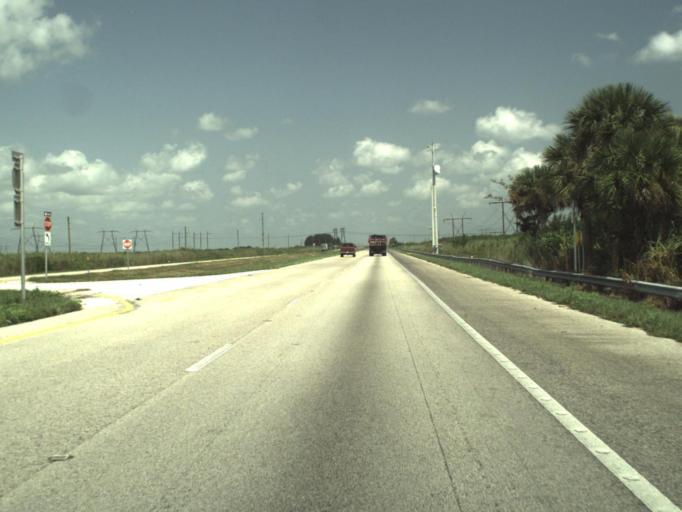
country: US
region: Florida
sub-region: Broward County
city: Weston
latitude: 26.3245
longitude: -80.5297
